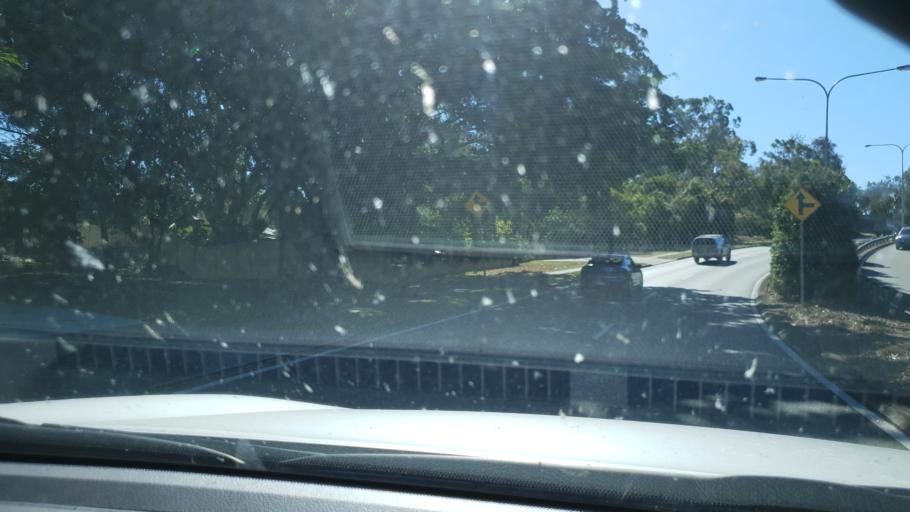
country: AU
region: Queensland
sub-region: Brisbane
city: Everton Park
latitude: -27.3929
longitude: 152.9850
